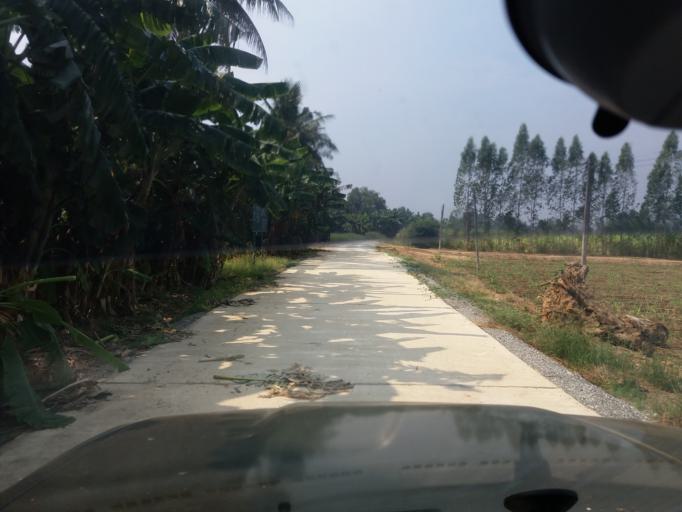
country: TH
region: Sing Buri
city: Bang Racham
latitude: 14.8984
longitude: 100.2155
